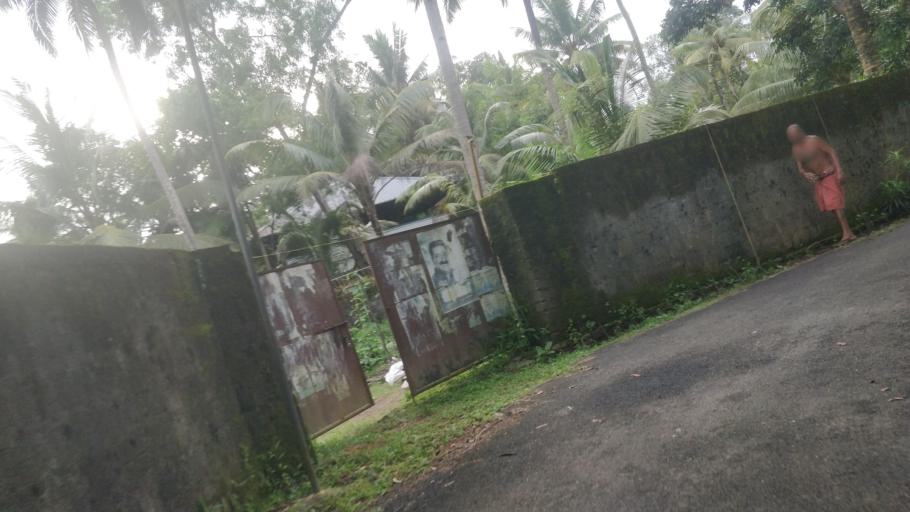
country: IN
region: Kerala
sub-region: Alappuzha
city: Shertallai
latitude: 9.6977
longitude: 76.3610
